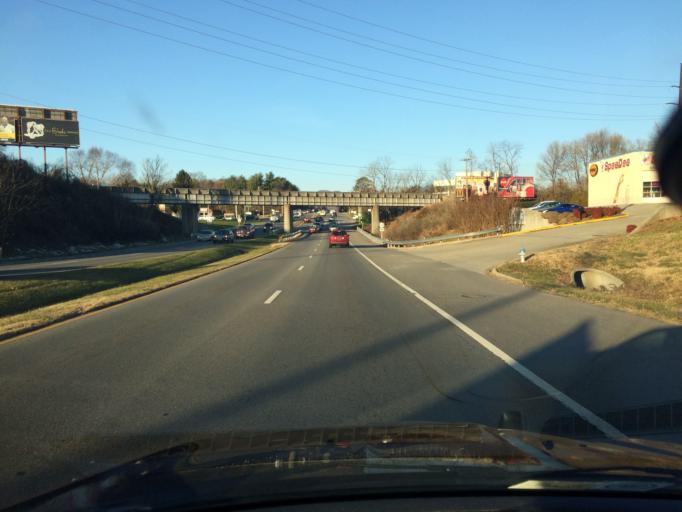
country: US
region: Virginia
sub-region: Roanoke County
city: Cave Spring
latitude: 37.2242
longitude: -79.9887
